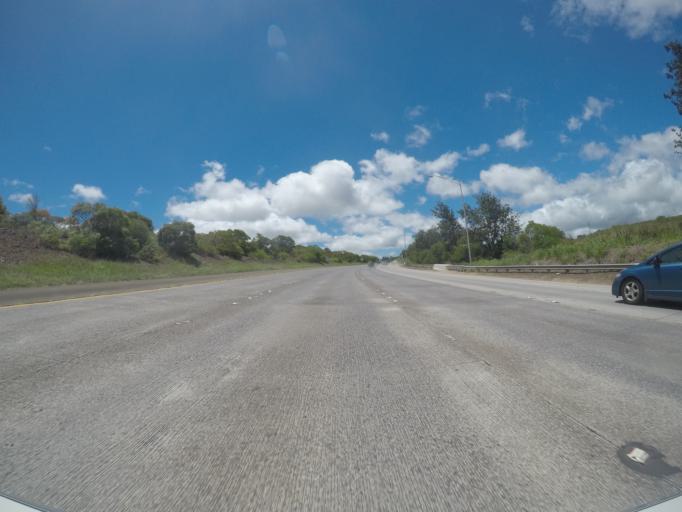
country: US
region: Hawaii
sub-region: Honolulu County
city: Waipio
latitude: 21.4170
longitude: -157.9933
